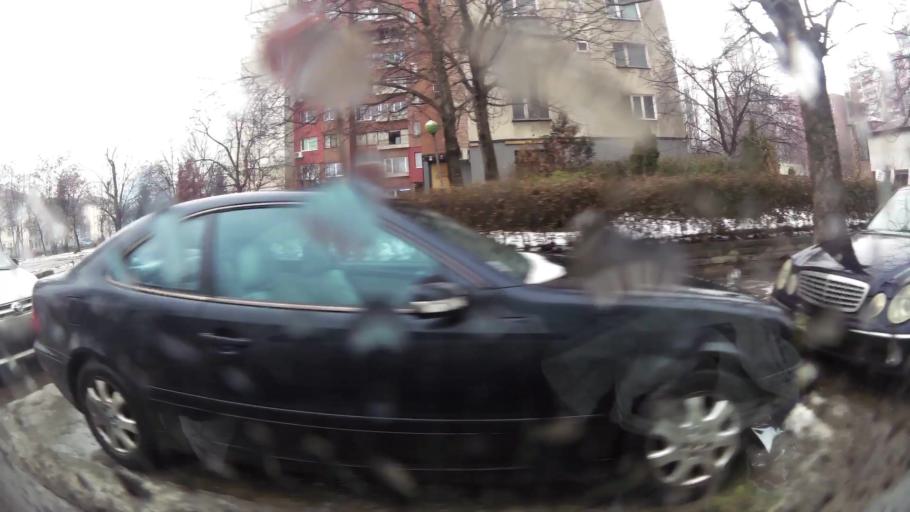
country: BG
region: Sofia-Capital
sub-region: Stolichna Obshtina
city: Sofia
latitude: 42.6751
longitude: 23.2956
